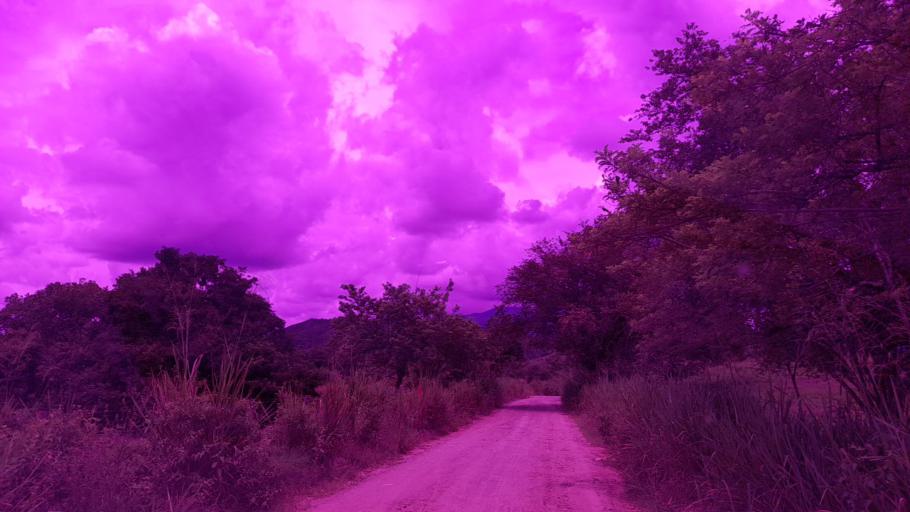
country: CO
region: Valle del Cauca
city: Andalucia
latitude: 4.1799
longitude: -76.1360
